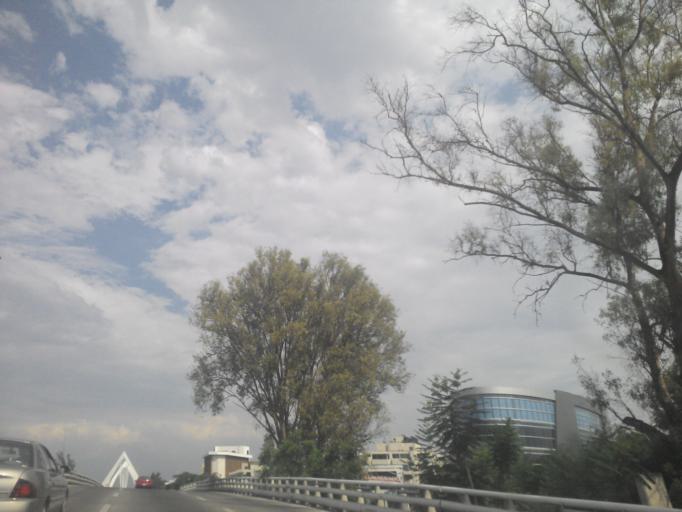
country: MX
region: Jalisco
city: Guadalajara
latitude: 20.6671
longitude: -103.3981
